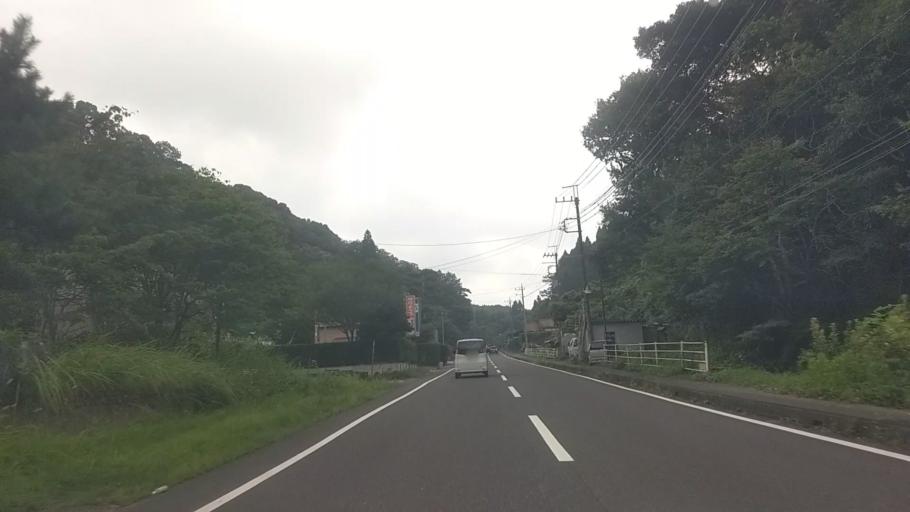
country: JP
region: Chiba
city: Kawaguchi
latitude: 35.2443
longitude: 140.1744
